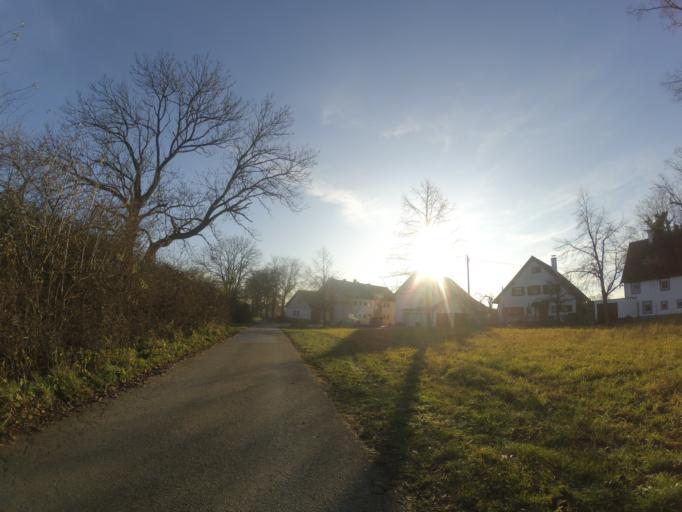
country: DE
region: Baden-Wuerttemberg
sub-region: Tuebingen Region
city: Dornstadt
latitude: 48.4455
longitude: 9.8957
